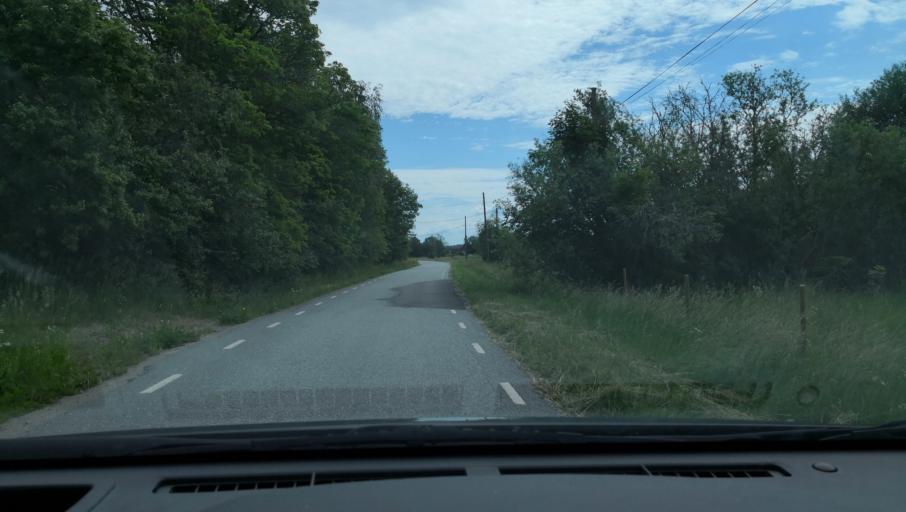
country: SE
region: Uppsala
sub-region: Enkopings Kommun
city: Orsundsbro
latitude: 59.6951
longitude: 17.4415
